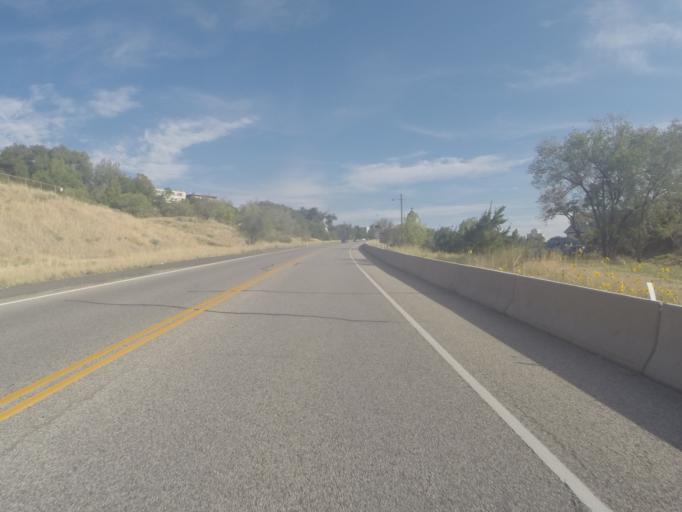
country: US
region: Utah
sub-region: Salt Lake County
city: Salt Lake City
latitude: 40.7836
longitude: -111.8926
